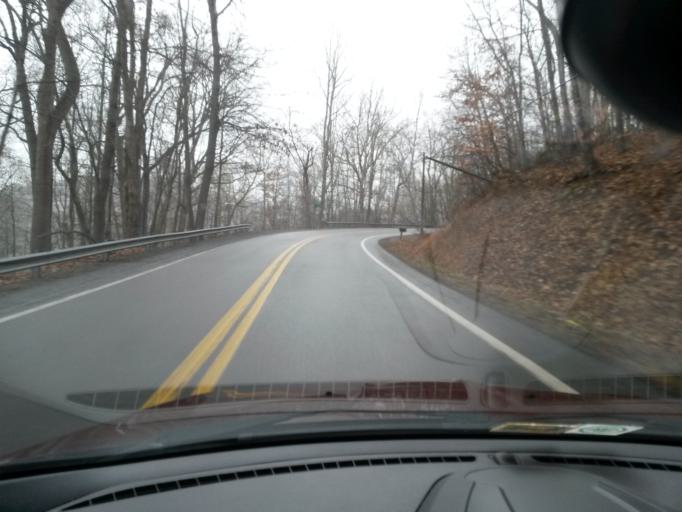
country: US
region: West Virginia
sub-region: Greenbrier County
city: Lewisburg
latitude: 37.8717
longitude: -80.5353
